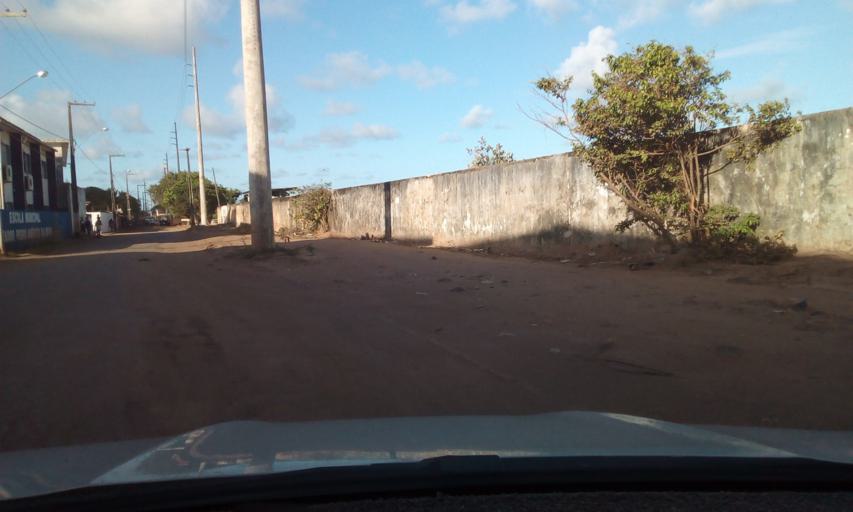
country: BR
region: Paraiba
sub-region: Cabedelo
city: Cabedelo
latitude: -7.0373
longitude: -34.8507
